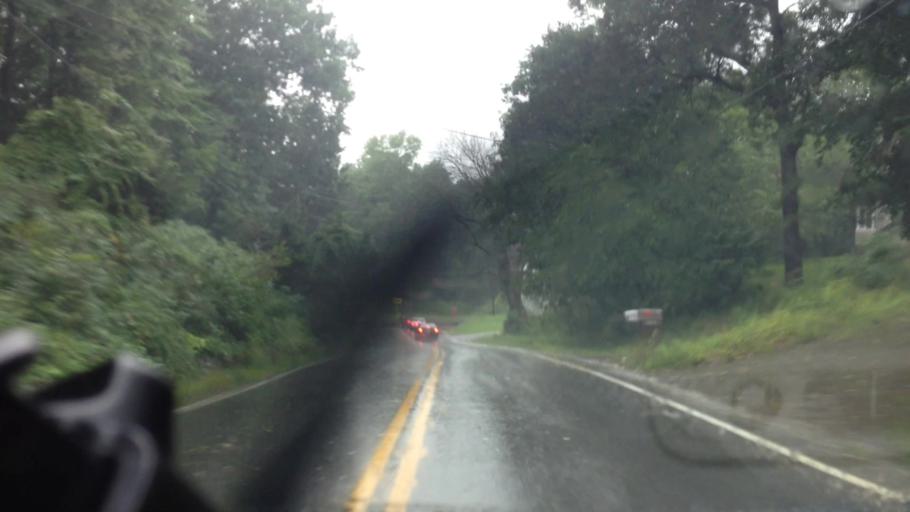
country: US
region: Ohio
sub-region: Stark County
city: Massillon
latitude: 40.8381
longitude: -81.5208
